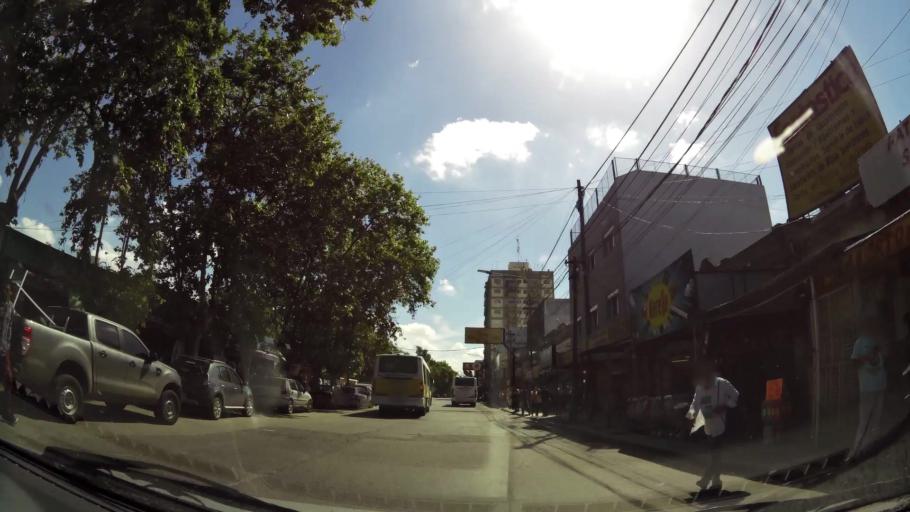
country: AR
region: Buenos Aires
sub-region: Partido de Quilmes
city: Quilmes
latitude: -34.8107
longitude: -58.2730
